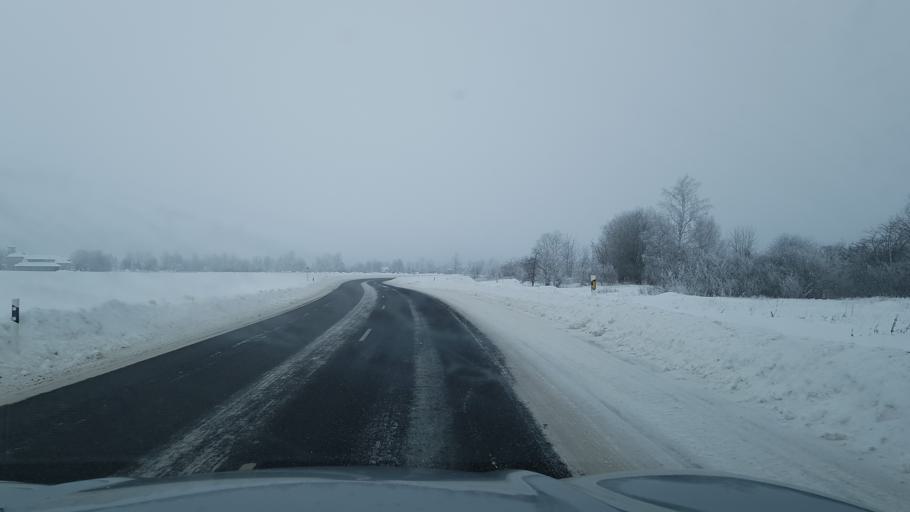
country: EE
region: Ida-Virumaa
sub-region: Johvi vald
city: Johvi
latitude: 59.3254
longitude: 27.3998
